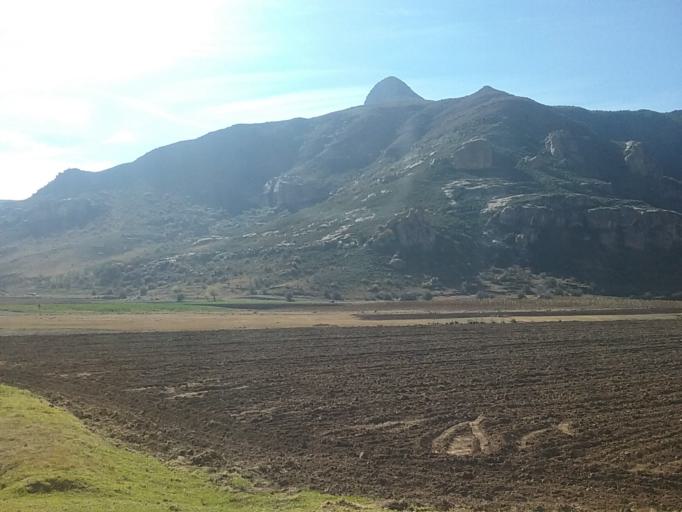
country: LS
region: Berea
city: Teyateyaneng
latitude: -29.2509
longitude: 27.9138
